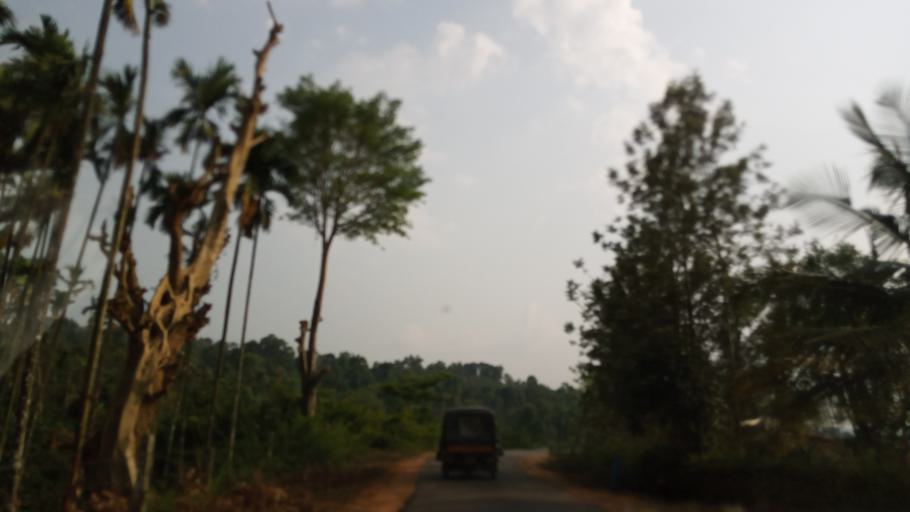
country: IN
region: Karnataka
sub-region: Chikmagalur
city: Mudigere
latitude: 13.0580
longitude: 75.6602
